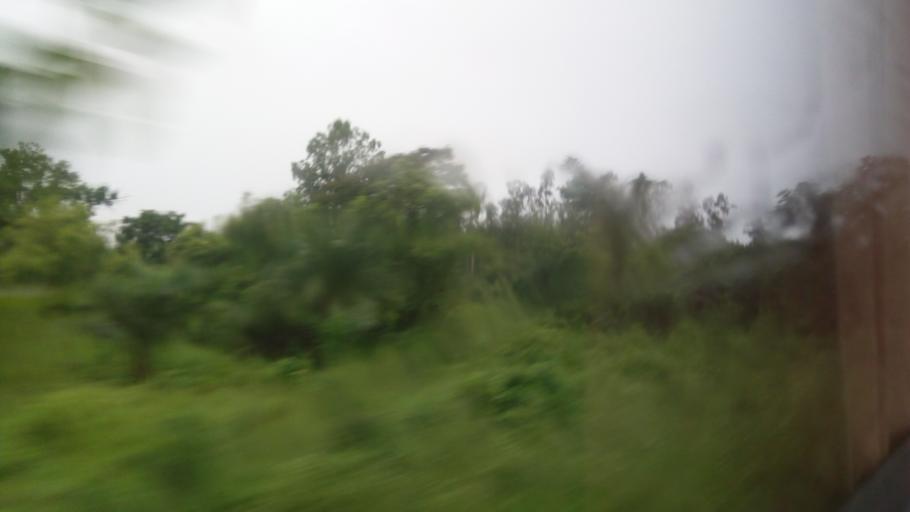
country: TG
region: Maritime
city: Tsevie
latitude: 6.5430
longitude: 1.1864
